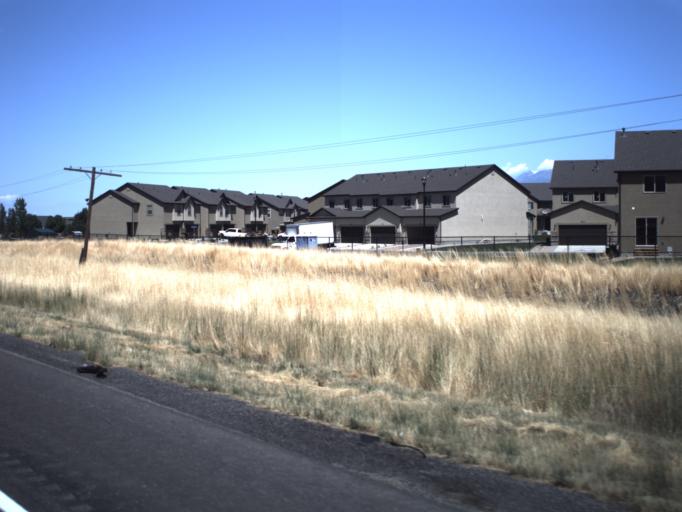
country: US
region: Utah
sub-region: Utah County
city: Spanish Fork
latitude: 40.1052
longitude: -111.6232
